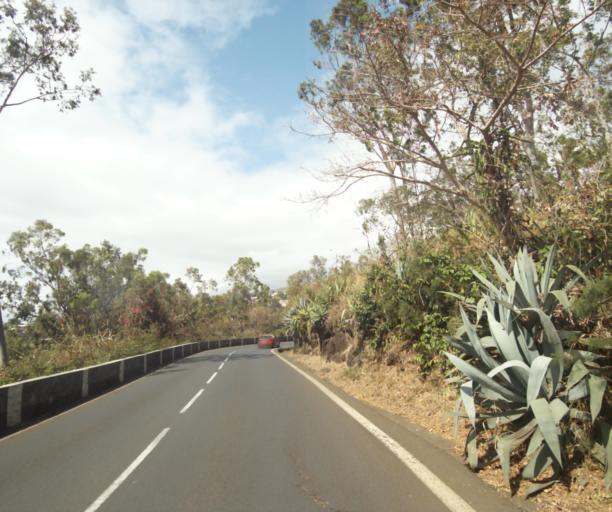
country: RE
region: Reunion
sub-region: Reunion
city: Saint-Paul
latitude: -21.0547
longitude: 55.2657
